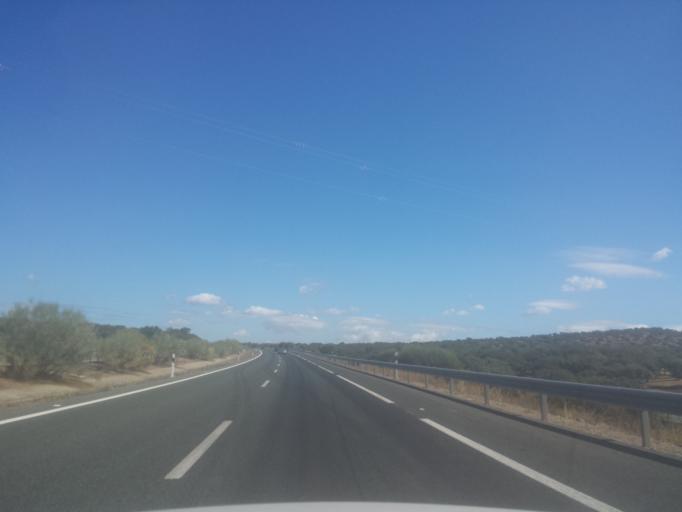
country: ES
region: Andalusia
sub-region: Provincia de Huelva
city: Santa Olalla del Cala
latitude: 37.8603
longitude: -6.2179
